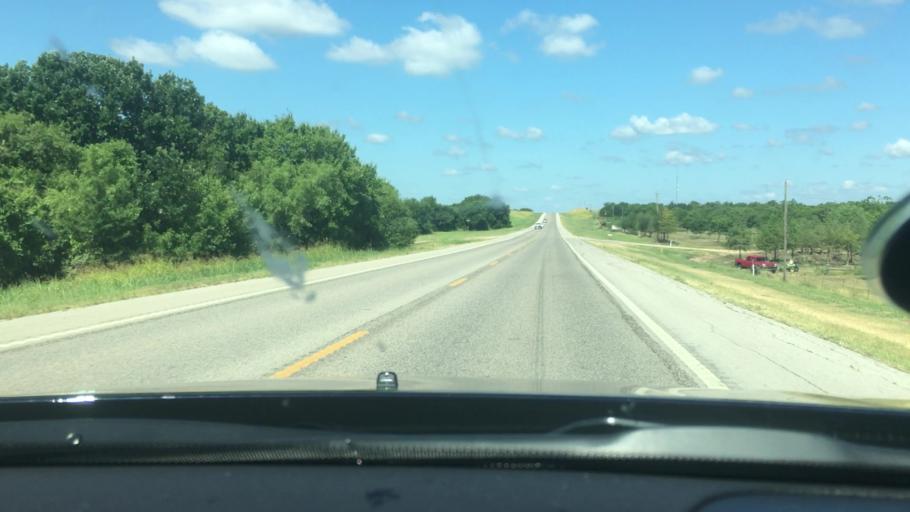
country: US
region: Oklahoma
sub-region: Marshall County
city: Oakland
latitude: 34.0999
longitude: -96.8618
